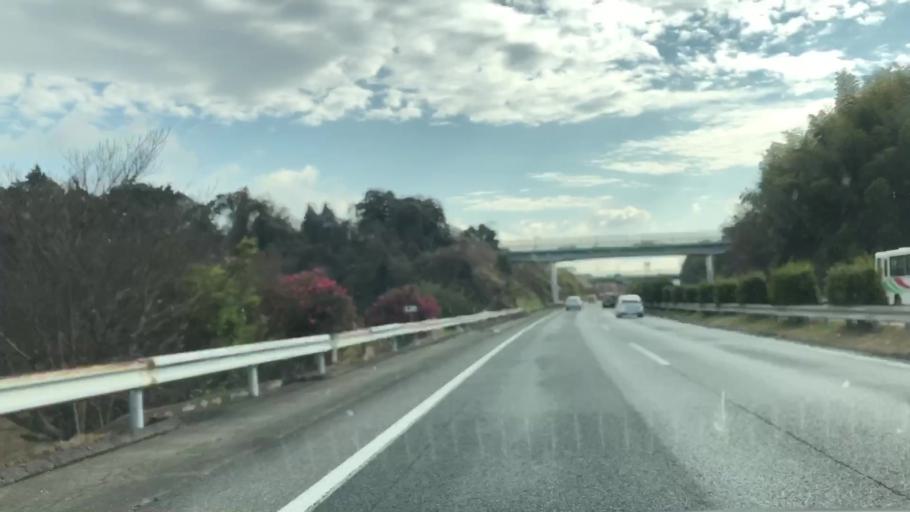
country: JP
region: Fukuoka
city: Setakamachi-takayanagi
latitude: 33.1345
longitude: 130.5165
